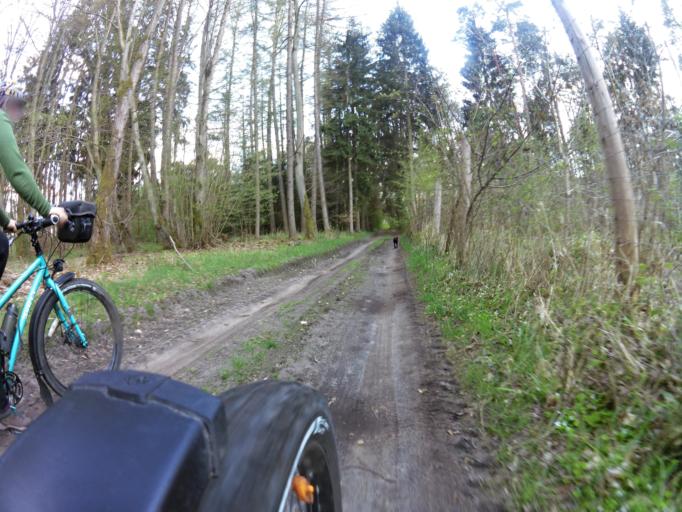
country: PL
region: West Pomeranian Voivodeship
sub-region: Powiat gryficki
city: Ploty
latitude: 53.7525
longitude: 15.2694
